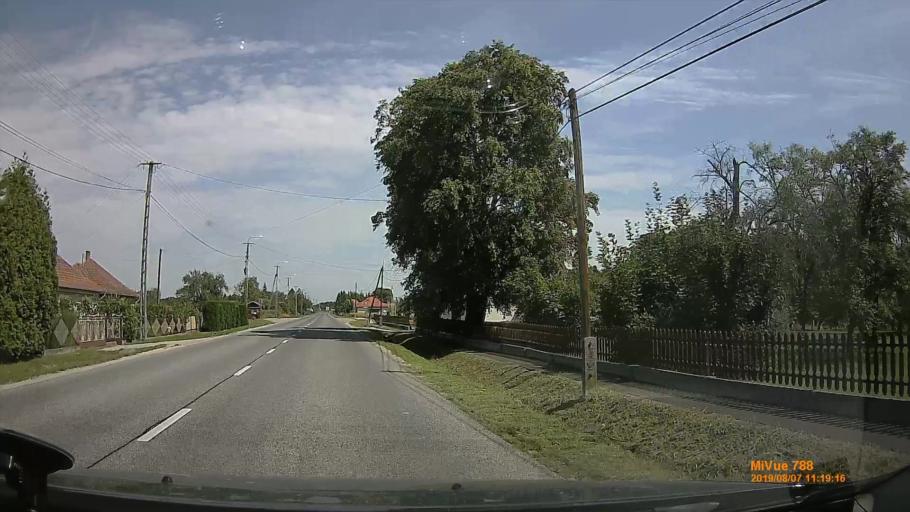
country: HU
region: Zala
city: Zalalovo
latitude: 46.7614
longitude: 16.5638
